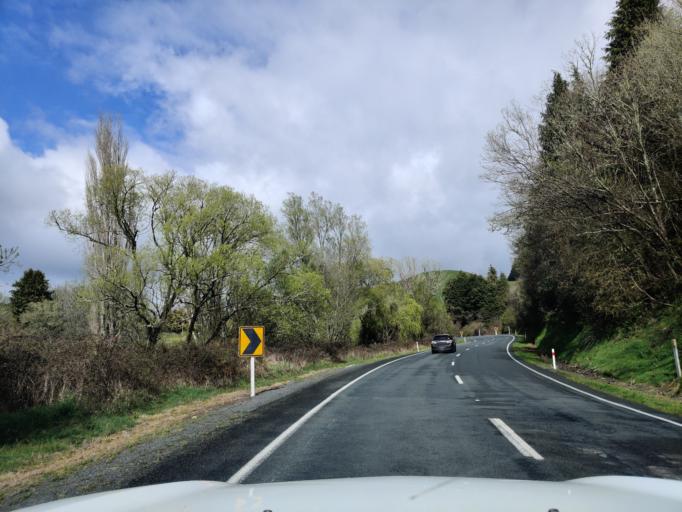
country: NZ
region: Waikato
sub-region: Otorohanga District
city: Otorohanga
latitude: -38.5969
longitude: 175.2185
